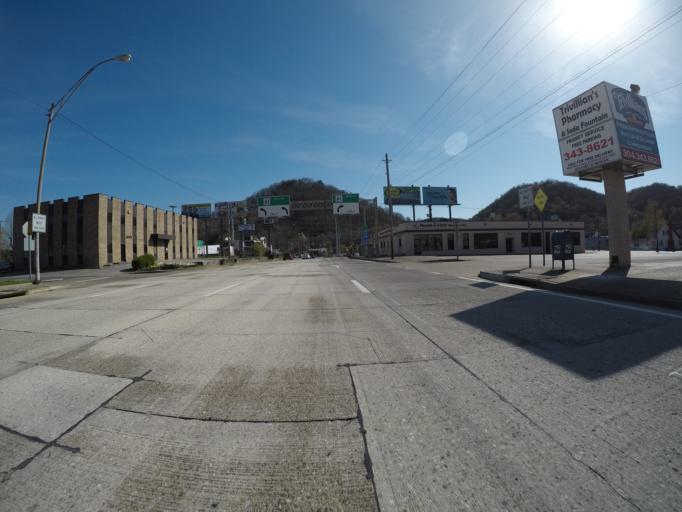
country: US
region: West Virginia
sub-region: Kanawha County
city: Charleston
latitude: 38.3294
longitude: -81.5984
